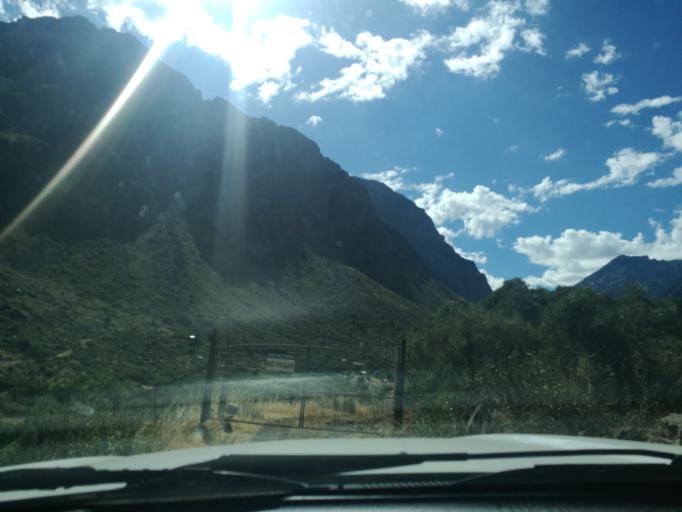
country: CL
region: O'Higgins
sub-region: Provincia de Cachapoal
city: Machali
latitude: -34.3882
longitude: -70.2797
